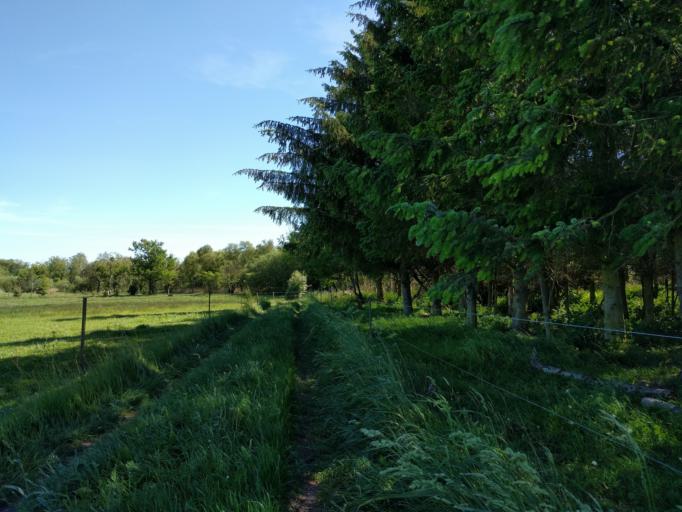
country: DK
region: South Denmark
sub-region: Kerteminde Kommune
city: Langeskov
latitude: 55.3849
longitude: 10.5902
